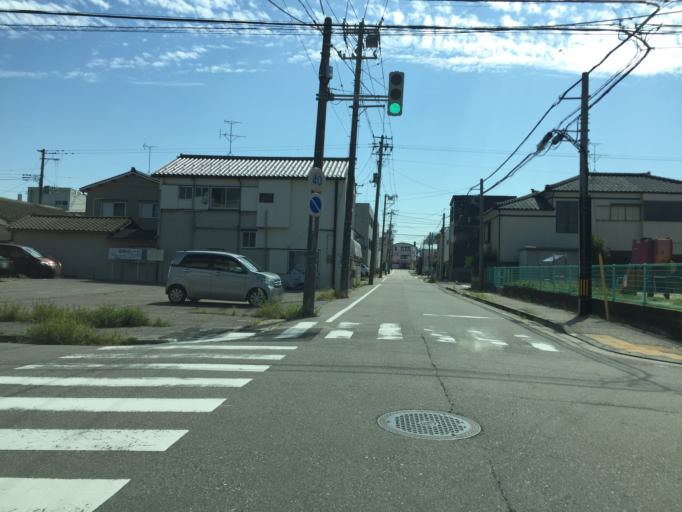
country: JP
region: Niigata
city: Niigata-shi
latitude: 37.9119
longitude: 139.0242
